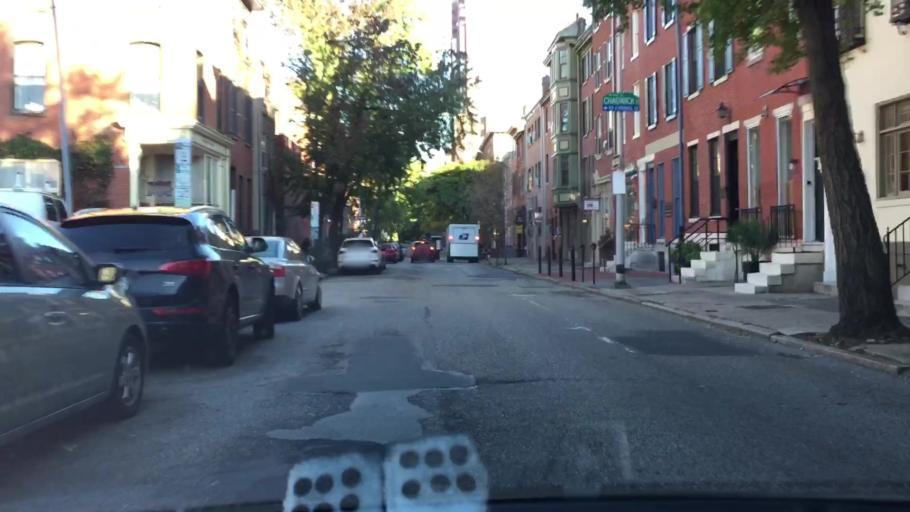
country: US
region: Pennsylvania
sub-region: Philadelphia County
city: Philadelphia
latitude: 39.9462
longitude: -75.1696
